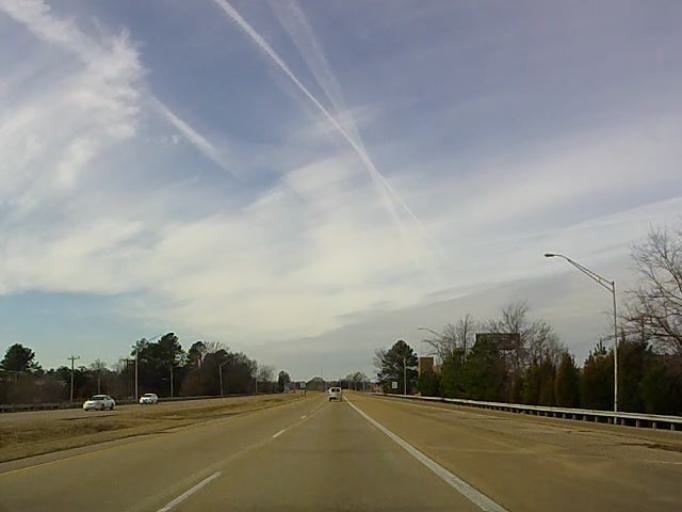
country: US
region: Tennessee
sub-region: Shelby County
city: Bartlett
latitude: 35.1483
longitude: -89.9480
